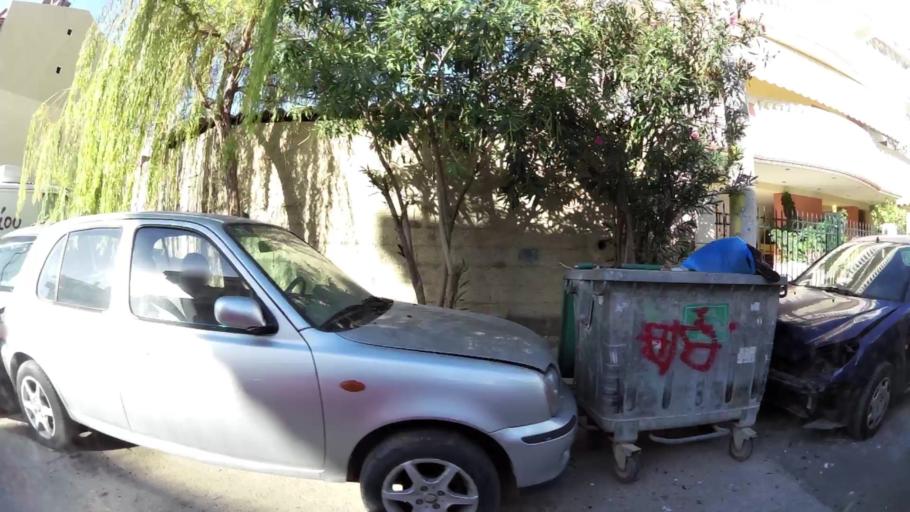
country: GR
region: Attica
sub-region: Nomarchia Anatolikis Attikis
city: Acharnes
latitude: 38.0671
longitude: 23.7401
